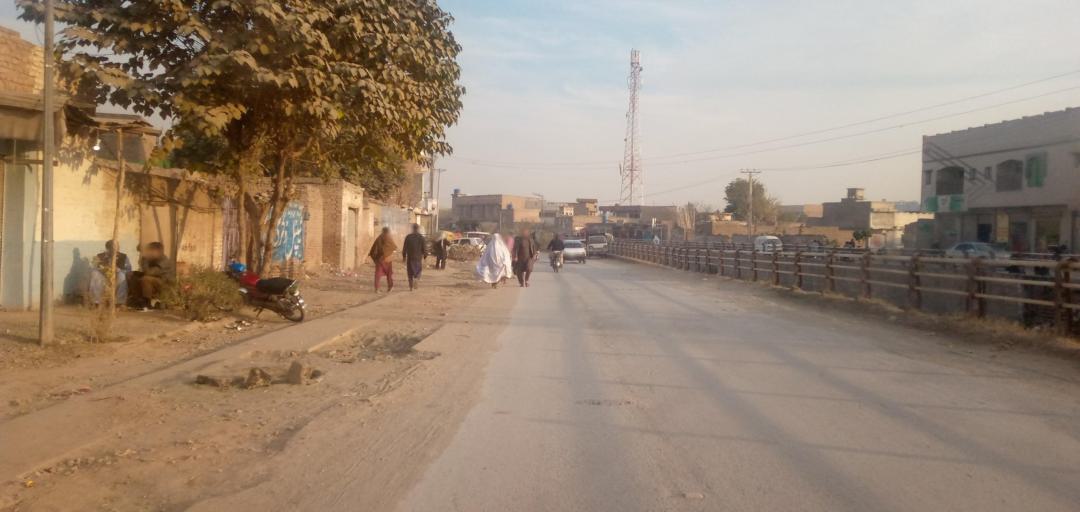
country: PK
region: Khyber Pakhtunkhwa
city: Peshawar
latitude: 33.9733
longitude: 71.5201
